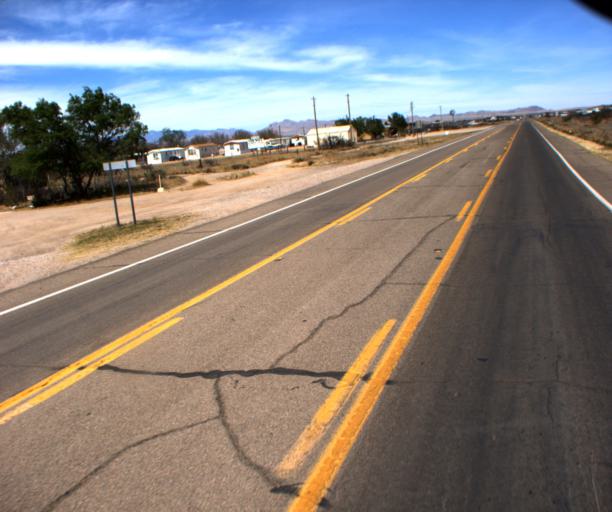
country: US
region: Arizona
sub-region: Cochise County
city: Willcox
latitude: 32.2621
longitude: -109.8259
